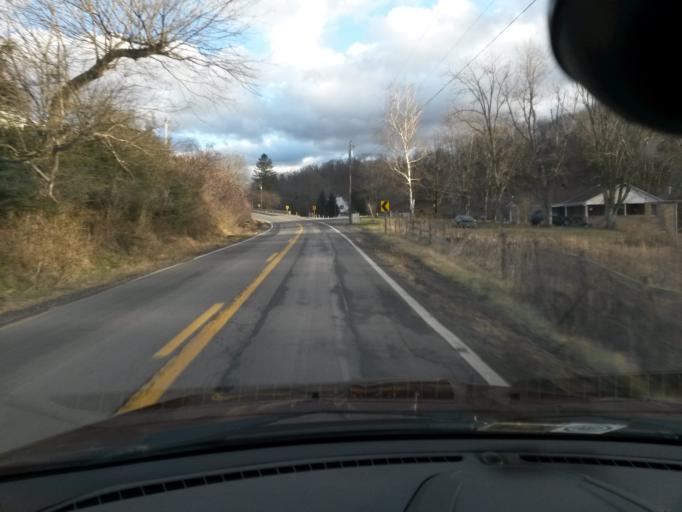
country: US
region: West Virginia
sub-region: Monroe County
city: Union
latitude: 37.5701
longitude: -80.5617
